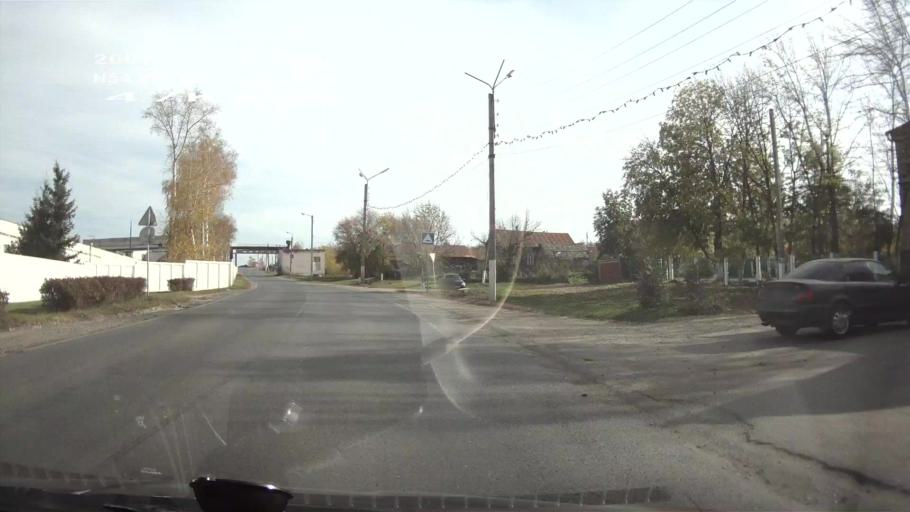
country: RU
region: Mordoviya
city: Turgenevo
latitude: 54.8460
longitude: 46.3385
